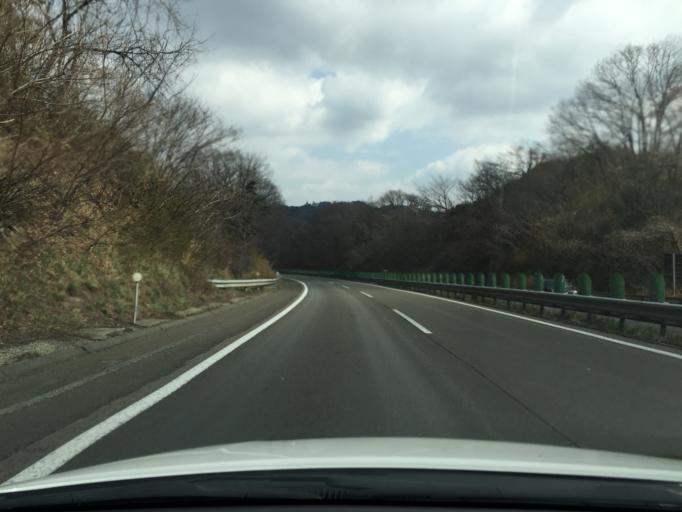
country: JP
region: Miyagi
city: Sendai
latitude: 38.2334
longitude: 140.8132
